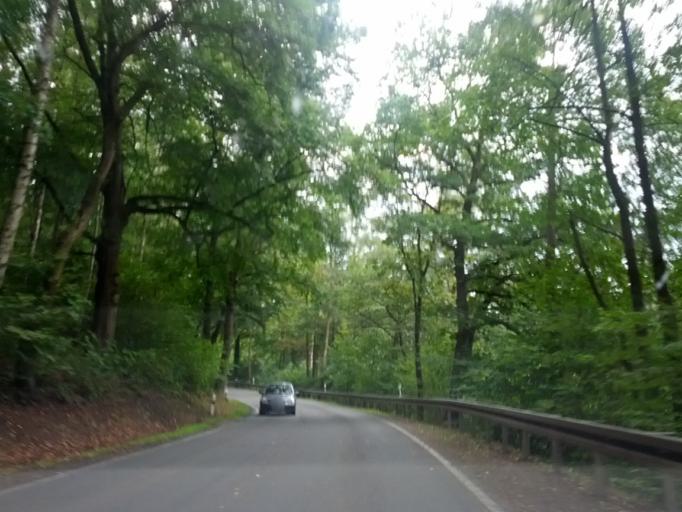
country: DE
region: Thuringia
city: Friedrichroda
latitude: 50.8721
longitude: 10.5647
